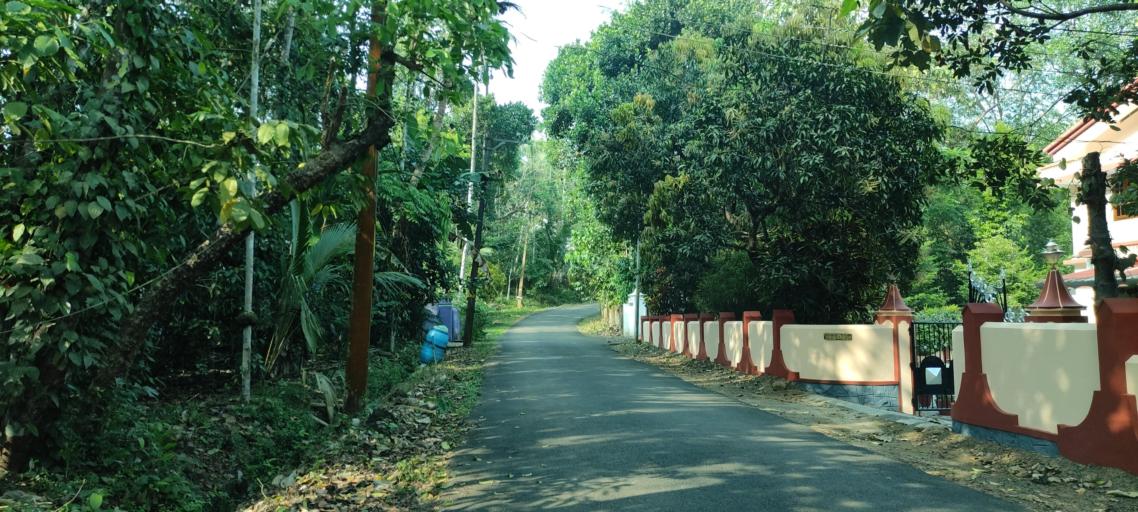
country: IN
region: Kerala
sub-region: Ernakulam
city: Piravam
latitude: 9.8034
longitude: 76.5255
